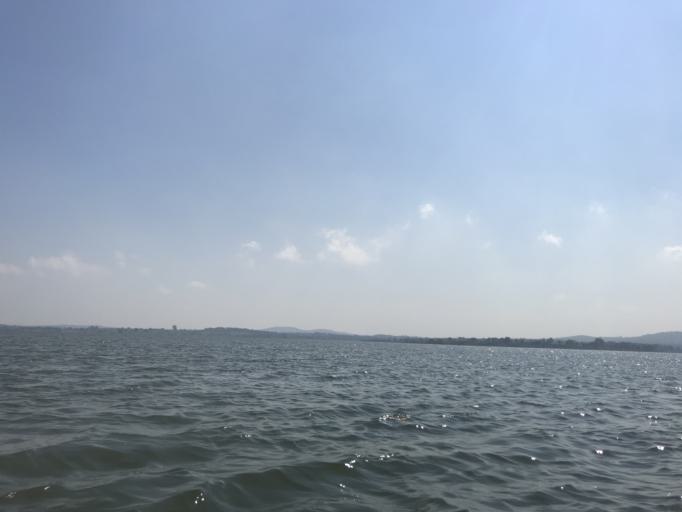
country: IN
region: Karnataka
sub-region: Mysore
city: Sargur
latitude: 11.9358
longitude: 76.2713
